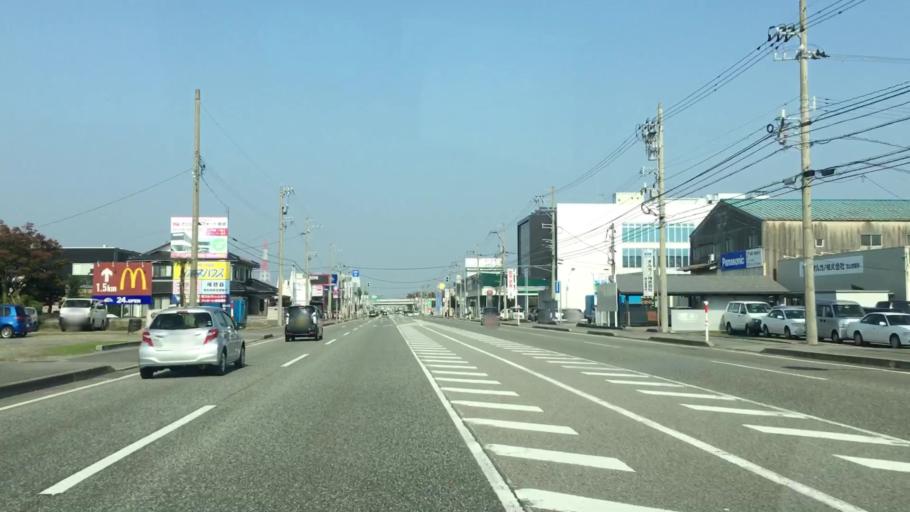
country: JP
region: Toyama
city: Toyama-shi
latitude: 36.6478
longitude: 137.2096
